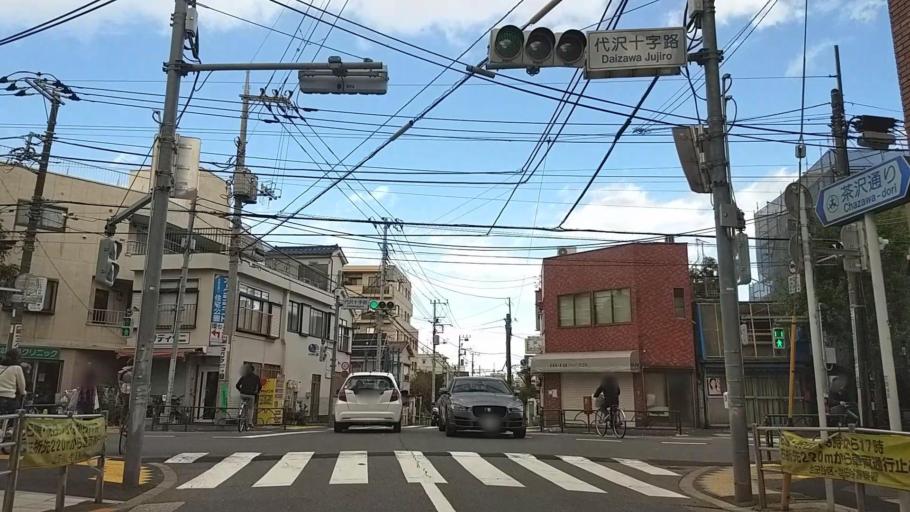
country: JP
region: Tokyo
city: Tokyo
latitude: 35.6508
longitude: 139.6673
